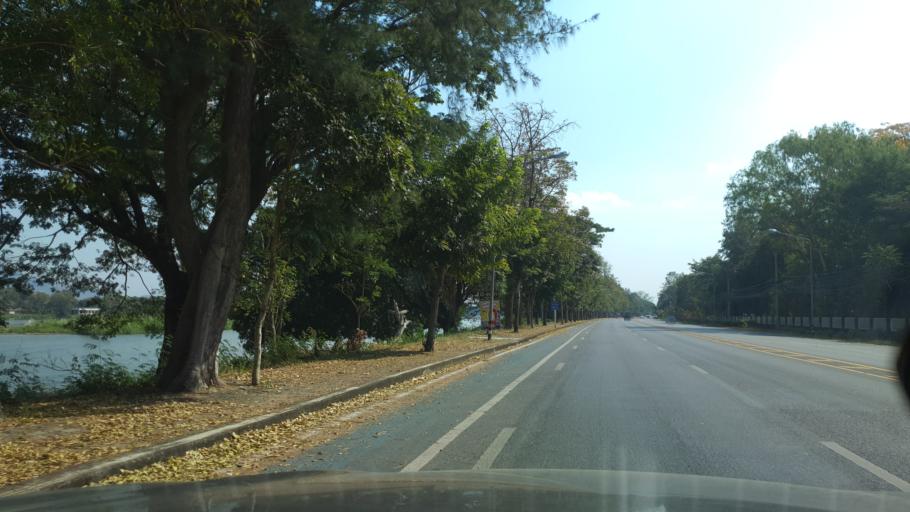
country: TH
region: Tak
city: Tak
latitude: 16.8740
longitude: 99.1176
